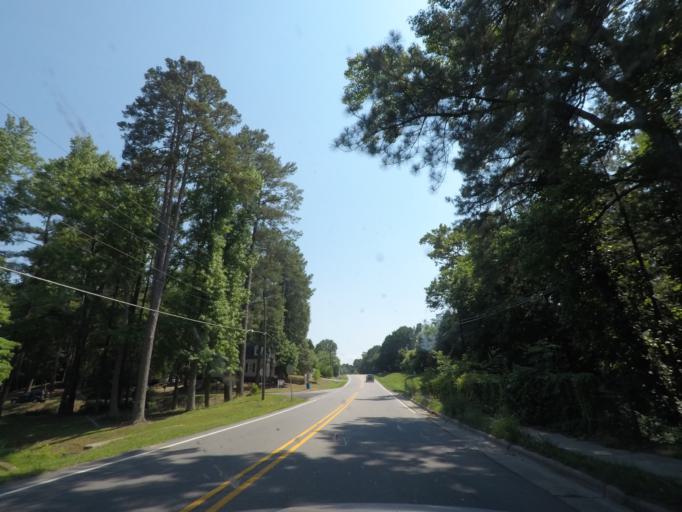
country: US
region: North Carolina
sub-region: Durham County
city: Durham
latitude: 35.9314
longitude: -78.9519
